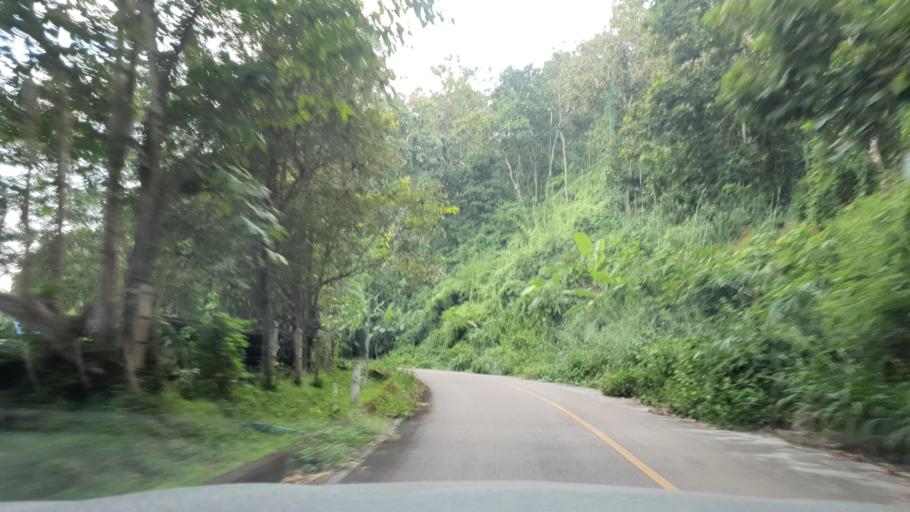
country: TH
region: Chiang Mai
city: Mae On
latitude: 18.8765
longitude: 99.2605
